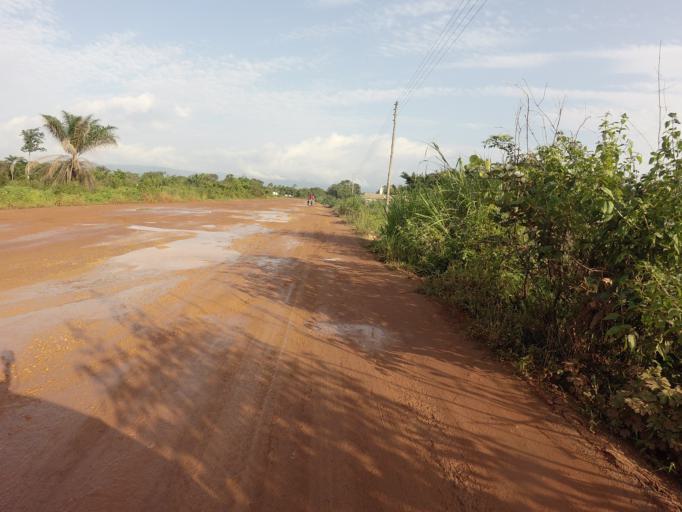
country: GH
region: Volta
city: Kpandu
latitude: 7.0091
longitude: 0.4291
